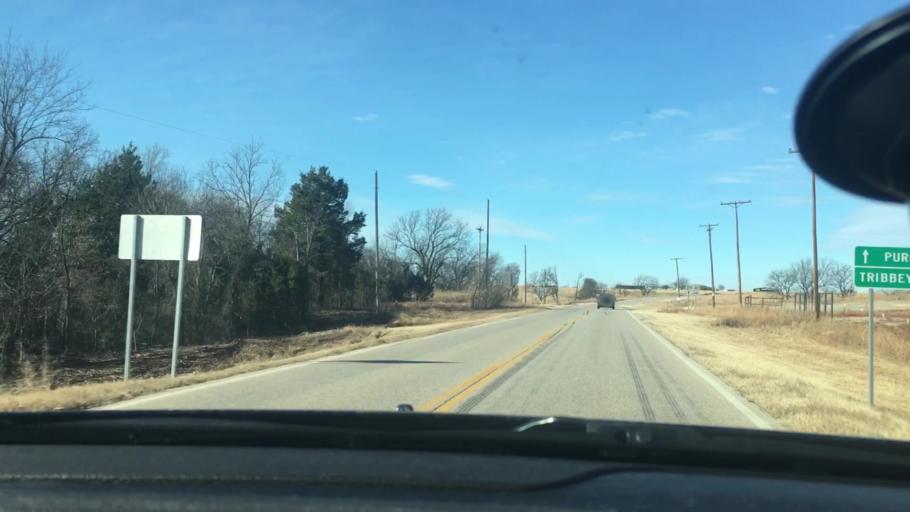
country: US
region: Oklahoma
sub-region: Garvin County
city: Stratford
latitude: 34.9858
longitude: -97.0353
